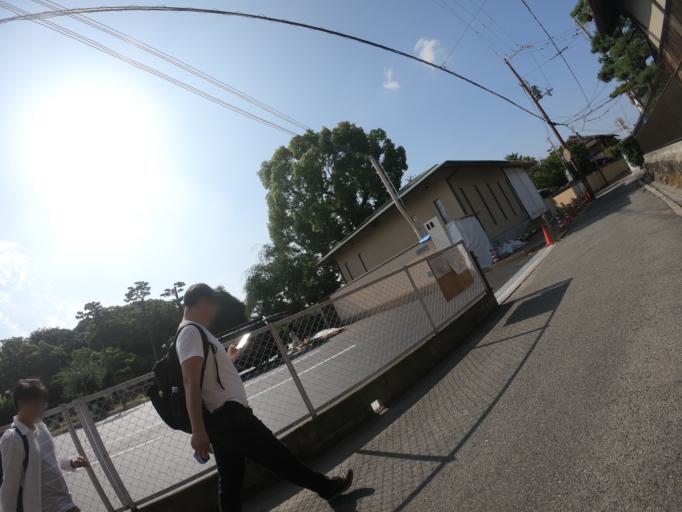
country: JP
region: Osaka
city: Sakai
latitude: 34.5762
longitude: 135.4897
